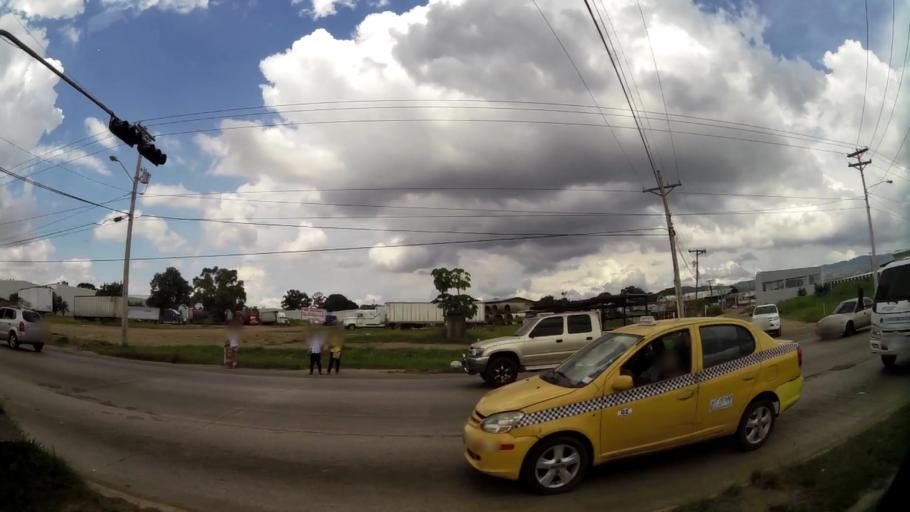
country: PA
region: Panama
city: Tocumen
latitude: 9.0841
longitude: -79.3982
